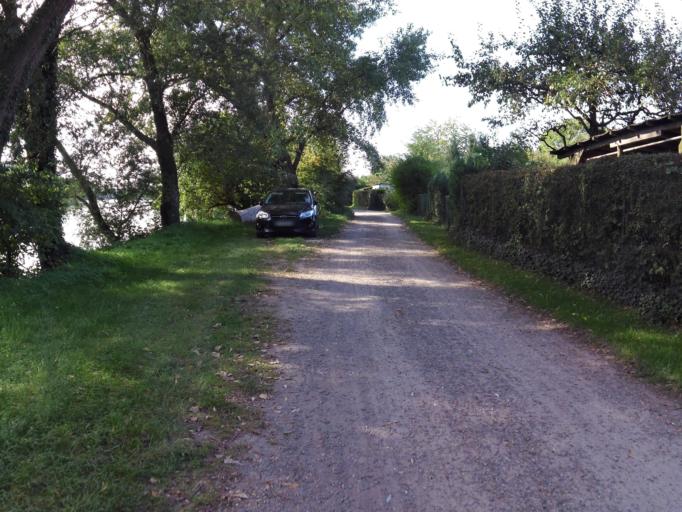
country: DE
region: Baden-Wuerttemberg
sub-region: Freiburg Region
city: Bad Sackingen
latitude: 47.5458
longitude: 7.9393
